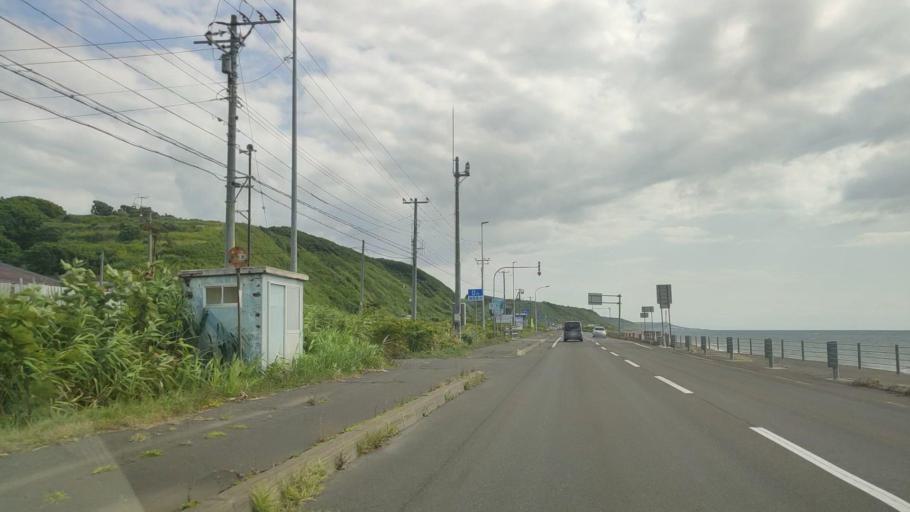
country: JP
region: Hokkaido
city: Rumoi
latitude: 44.2091
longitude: 141.6569
